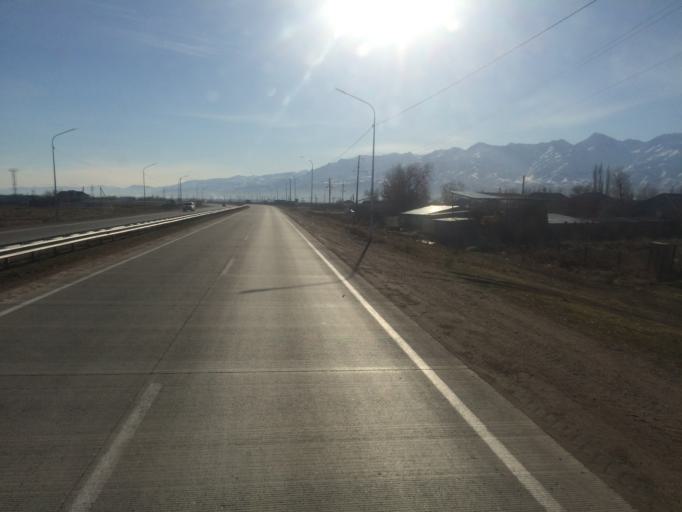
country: KG
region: Talas
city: Ivanovo-Alekseyevka
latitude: 42.9931
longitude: 72.1112
